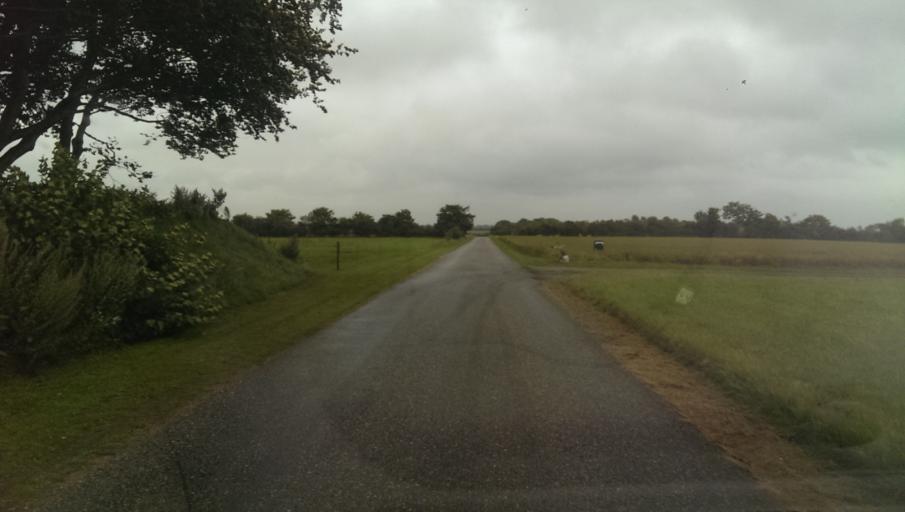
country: DK
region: South Denmark
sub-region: Esbjerg Kommune
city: Tjaereborg
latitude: 55.4871
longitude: 8.6089
